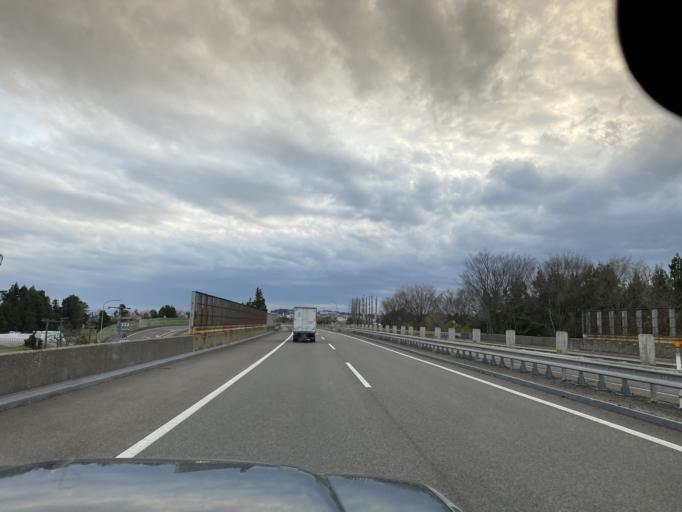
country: JP
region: Niigata
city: Nagaoka
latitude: 37.4600
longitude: 138.7919
